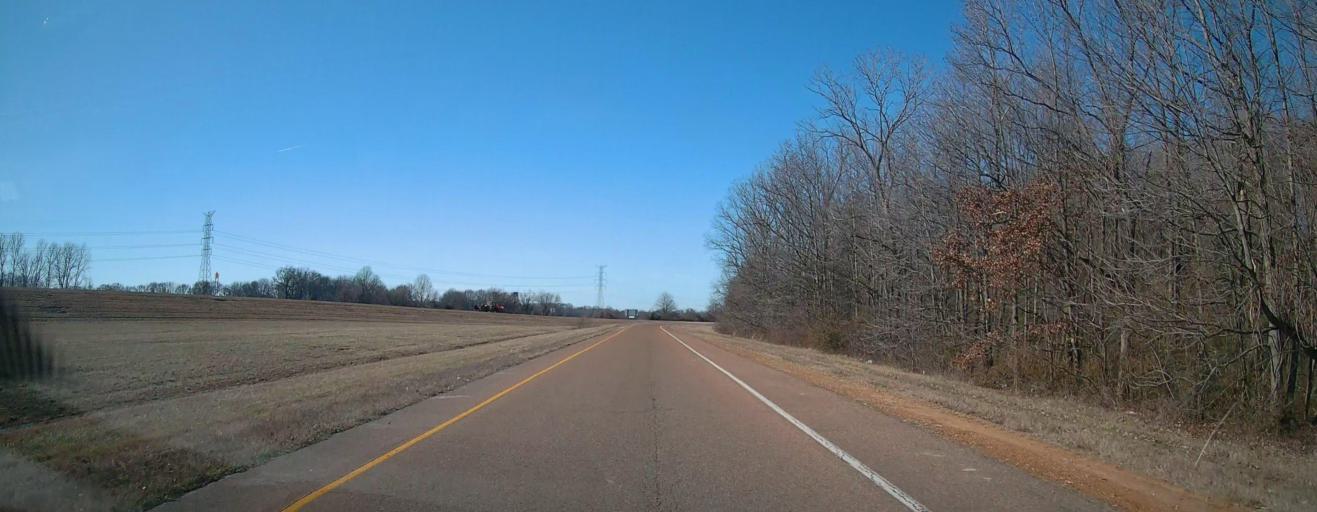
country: US
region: Tennessee
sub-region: Shelby County
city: Millington
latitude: 35.3210
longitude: -89.8732
